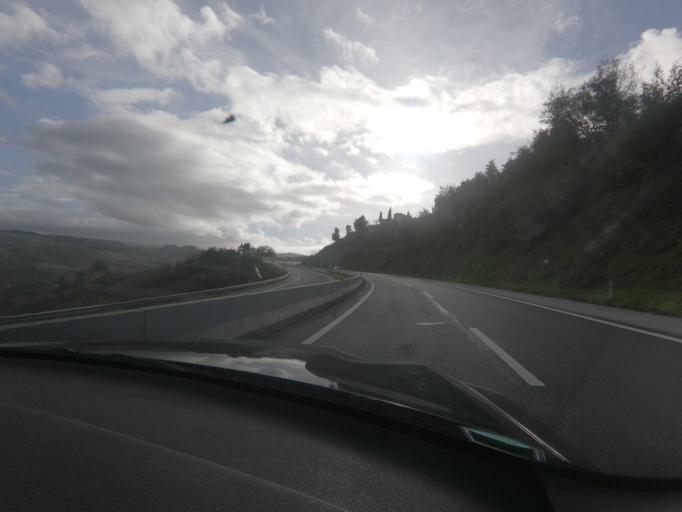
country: PT
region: Viseu
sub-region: Lamego
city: Lamego
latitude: 41.0957
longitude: -7.7829
